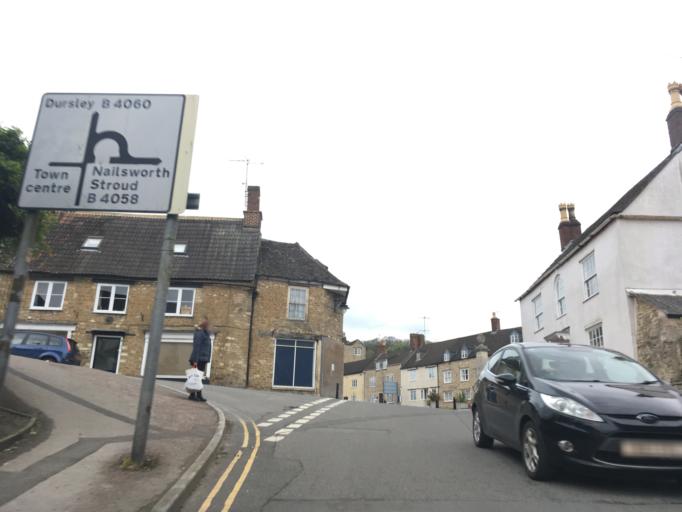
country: GB
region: England
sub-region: Gloucestershire
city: Wotton-under-Edge
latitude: 51.6384
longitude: -2.3495
